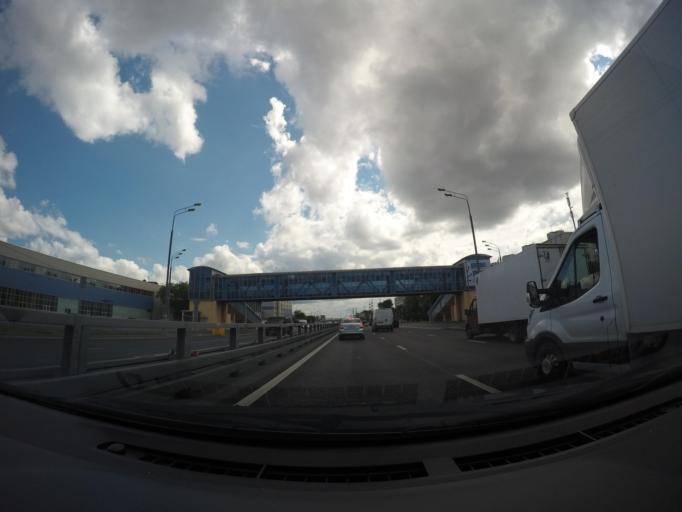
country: RU
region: Moscow
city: Veshnyaki
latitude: 55.7100
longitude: 37.8251
